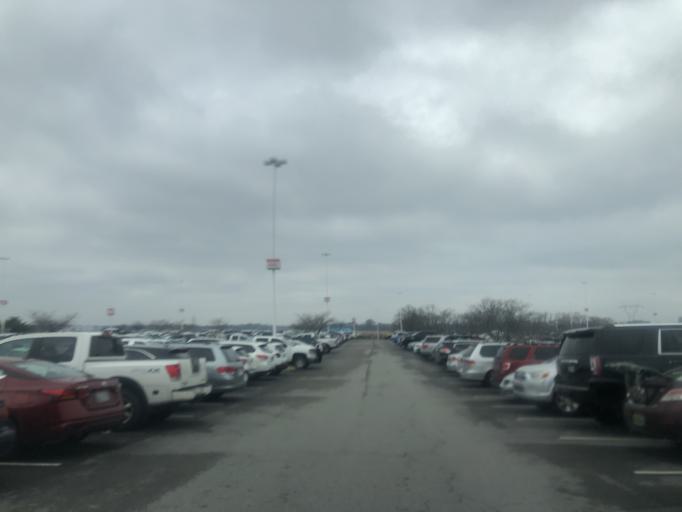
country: US
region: Tennessee
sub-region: Davidson County
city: Lakewood
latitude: 36.1383
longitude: -86.6667
